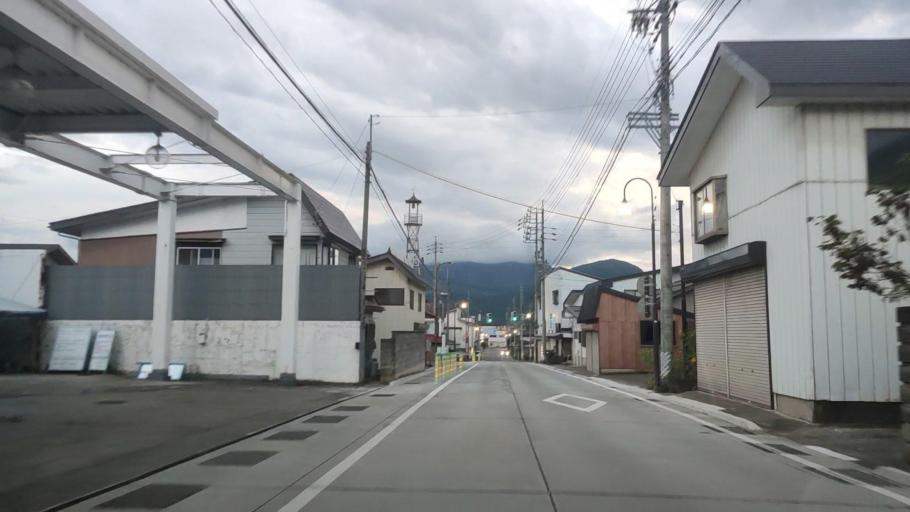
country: JP
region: Nagano
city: Iiyama
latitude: 36.8638
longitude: 138.4062
